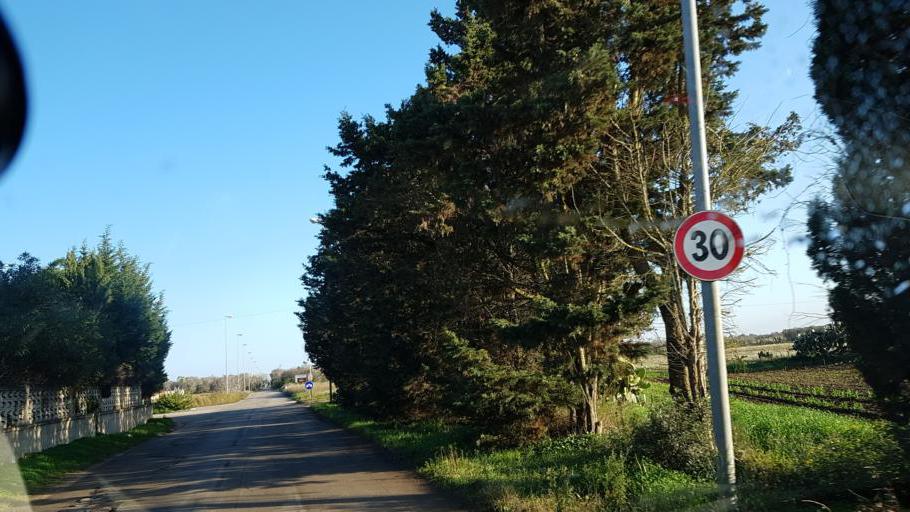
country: IT
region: Apulia
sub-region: Provincia di Brindisi
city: Torchiarolo
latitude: 40.5057
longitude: 18.1001
